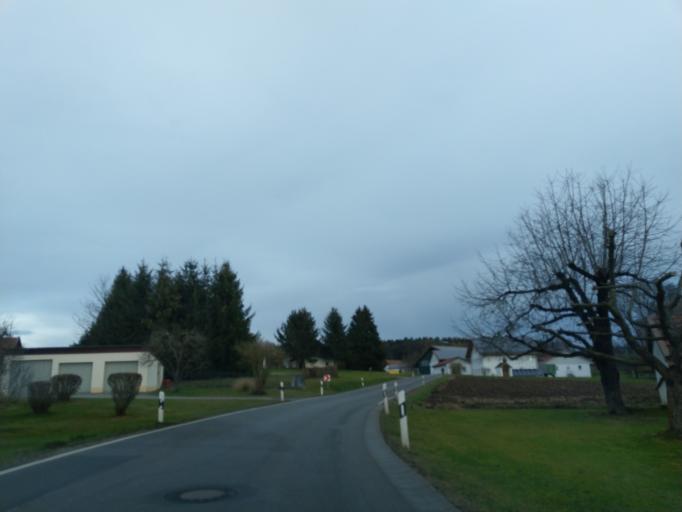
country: DE
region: Bavaria
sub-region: Lower Bavaria
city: Rossbach
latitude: 48.6357
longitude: 12.9655
